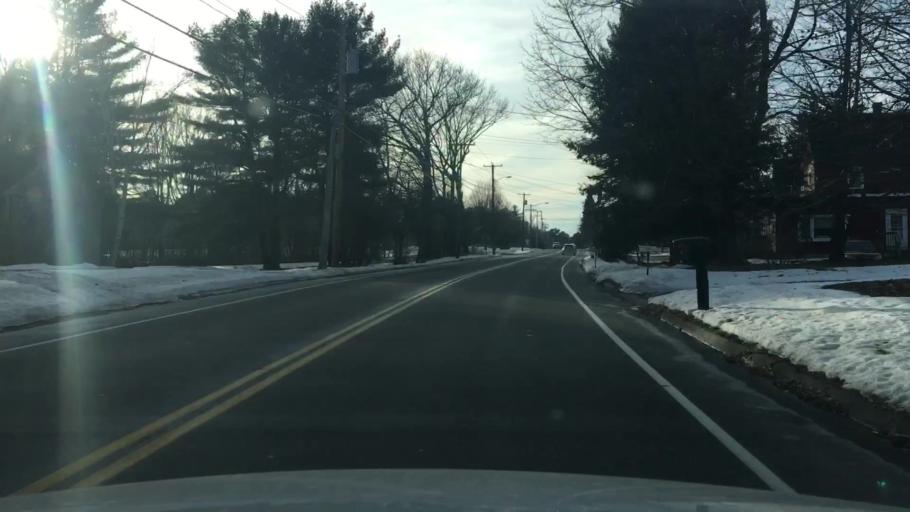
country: US
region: Maine
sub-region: York County
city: Wells Beach Station
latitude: 43.3217
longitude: -70.5916
